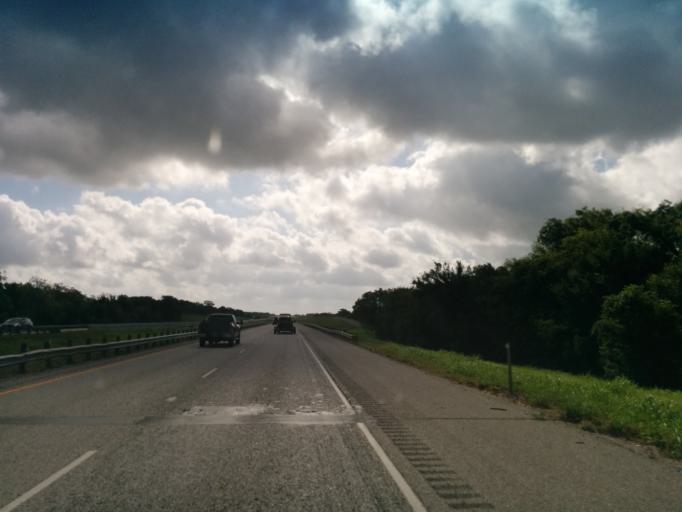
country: US
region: Texas
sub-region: Gonzales County
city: Waelder
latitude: 29.6626
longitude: -97.3813
